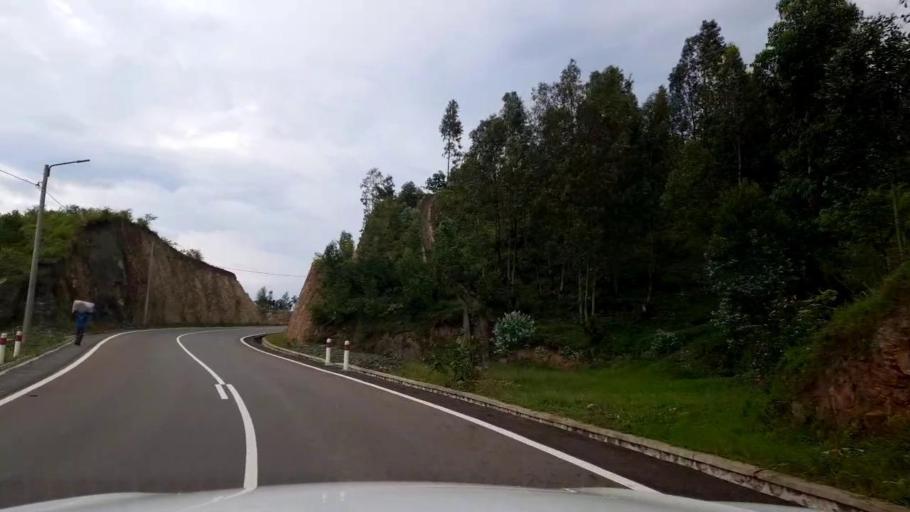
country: RW
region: Western Province
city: Kibuye
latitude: -2.0268
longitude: 29.3938
